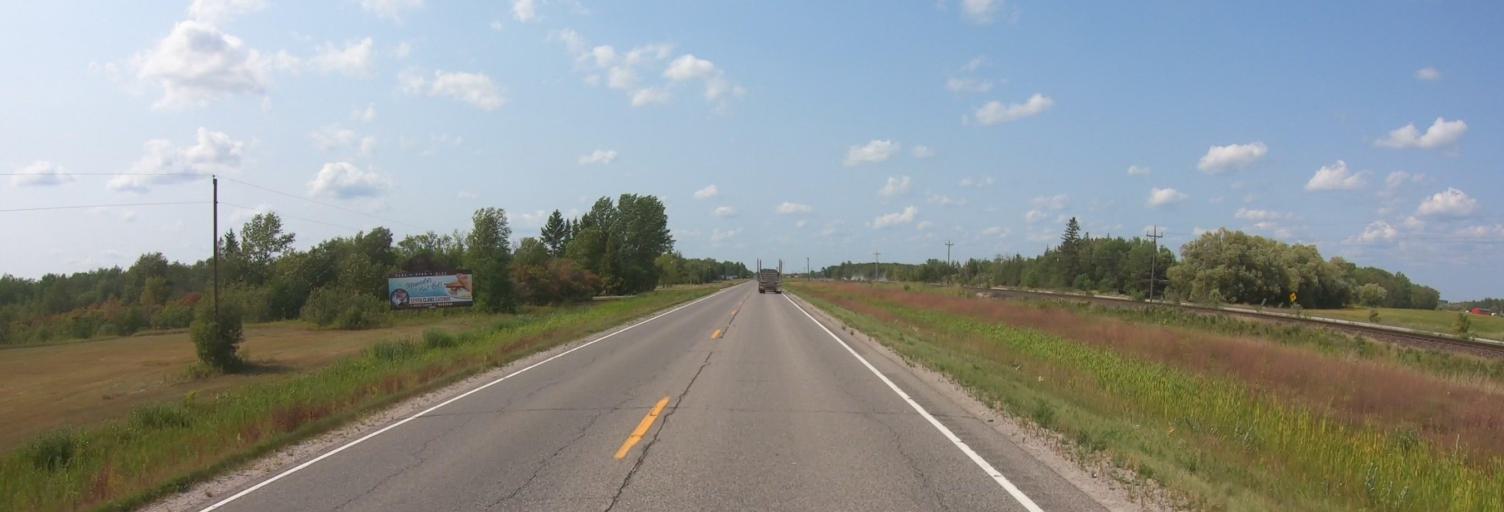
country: US
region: Minnesota
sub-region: Roseau County
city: Warroad
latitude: 48.8848
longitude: -95.2944
